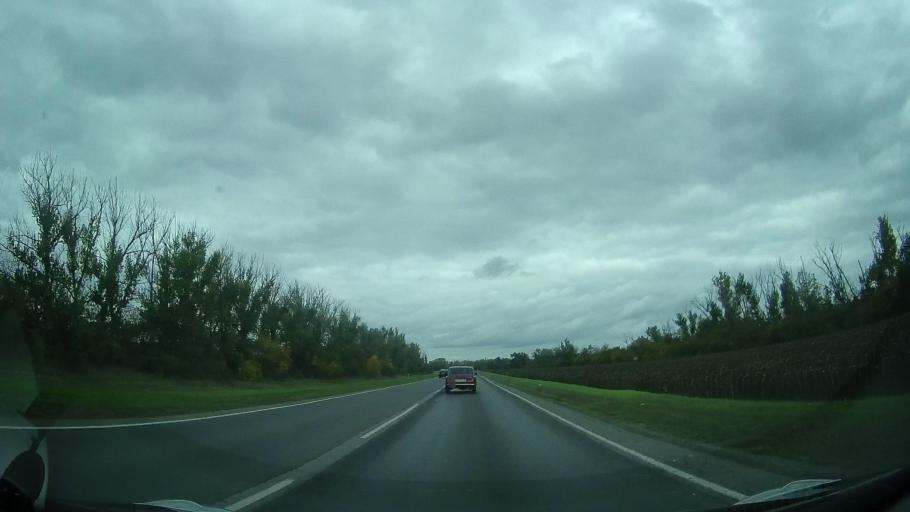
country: RU
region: Rostov
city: Yegorlykskaya
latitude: 46.5401
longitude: 40.7755
